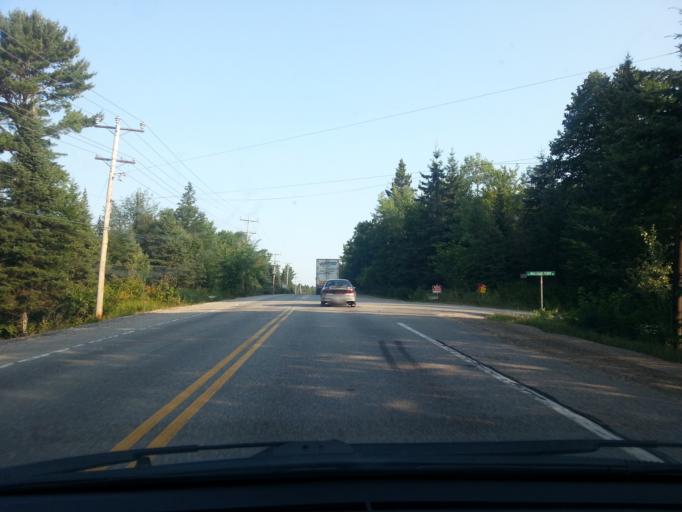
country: CA
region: Quebec
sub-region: Outaouais
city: Maniwaki
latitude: 46.0034
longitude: -76.0473
